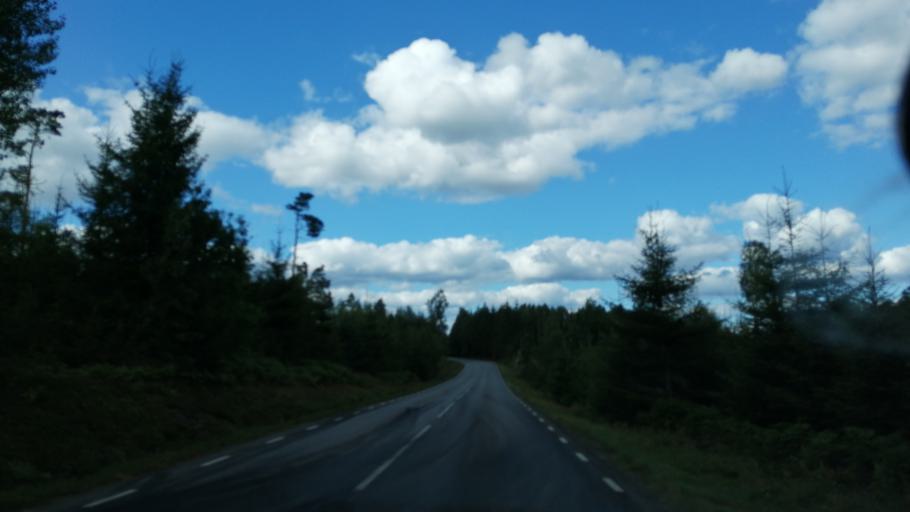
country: SE
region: Joenkoeping
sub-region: Varnamo Kommun
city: Bredaryd
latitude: 57.0762
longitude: 13.6816
